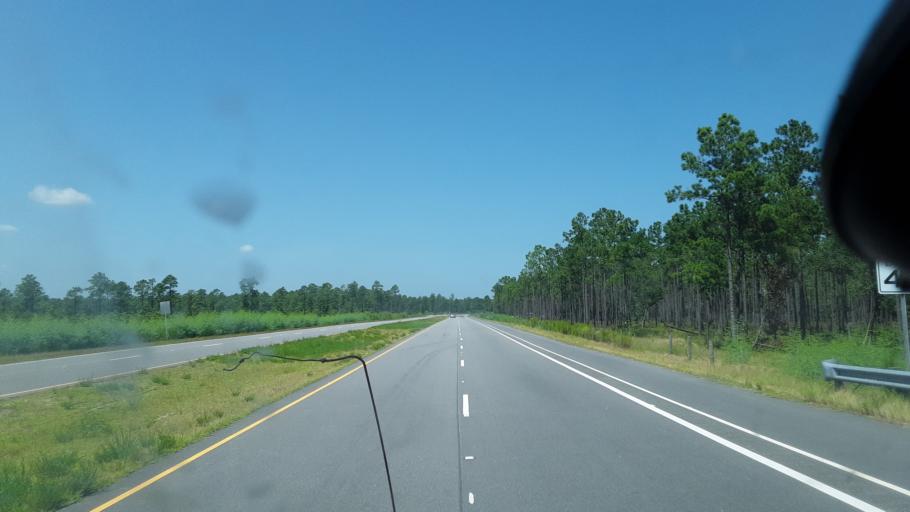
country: US
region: South Carolina
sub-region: Horry County
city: Forestbrook
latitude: 33.8038
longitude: -78.8876
